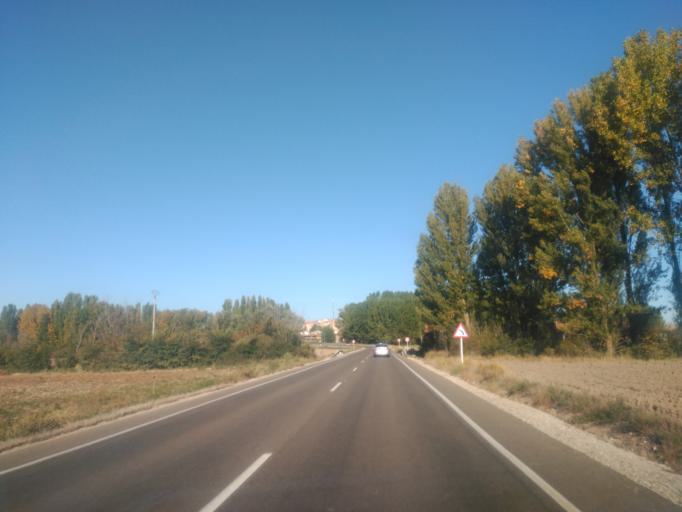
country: ES
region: Castille and Leon
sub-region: Provincia de Burgos
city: Quemada
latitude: 41.6989
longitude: -3.5684
